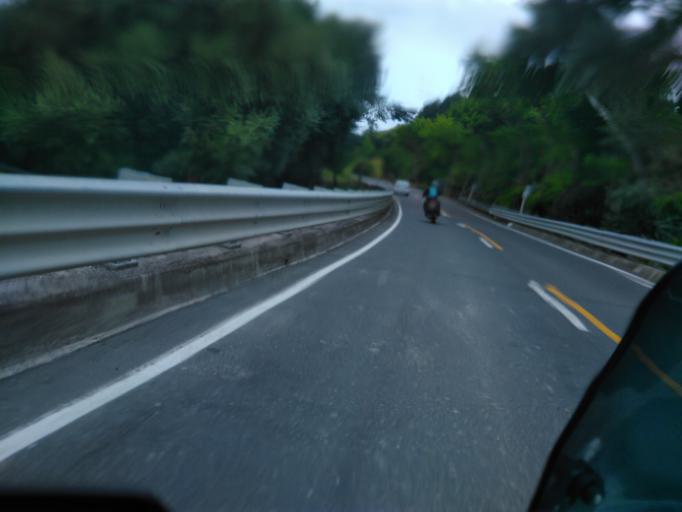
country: NZ
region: Gisborne
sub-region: Gisborne District
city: Gisborne
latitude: -38.4659
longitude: 177.8136
